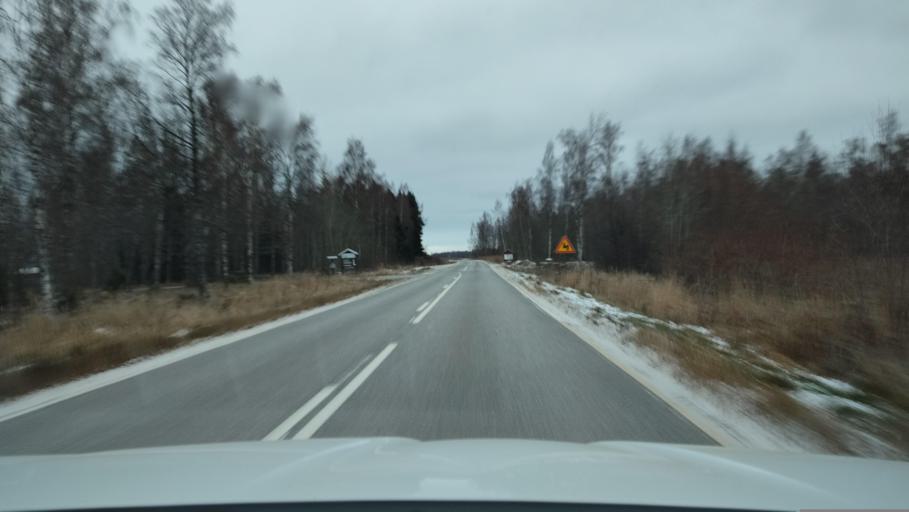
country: FI
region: Ostrobothnia
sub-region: Vaasa
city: Replot
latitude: 63.2783
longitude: 21.3417
